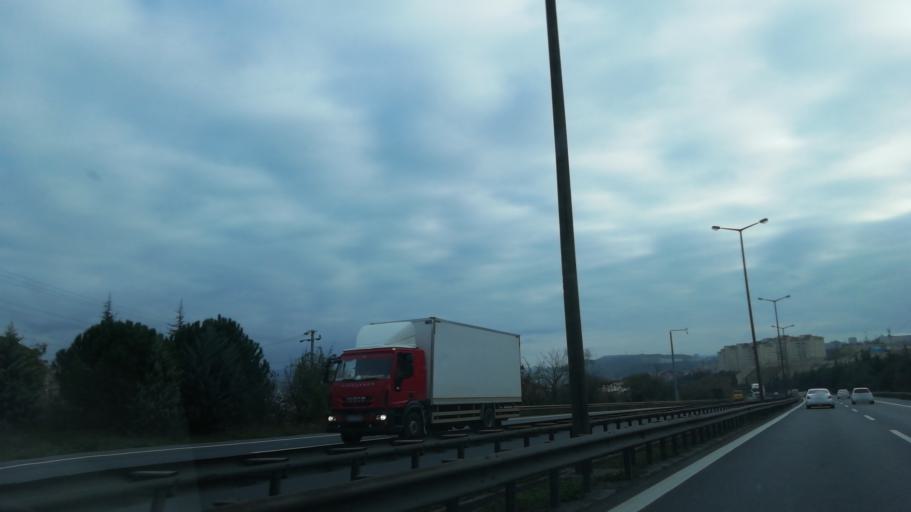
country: TR
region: Kocaeli
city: Izmit
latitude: 40.7856
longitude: 29.9555
